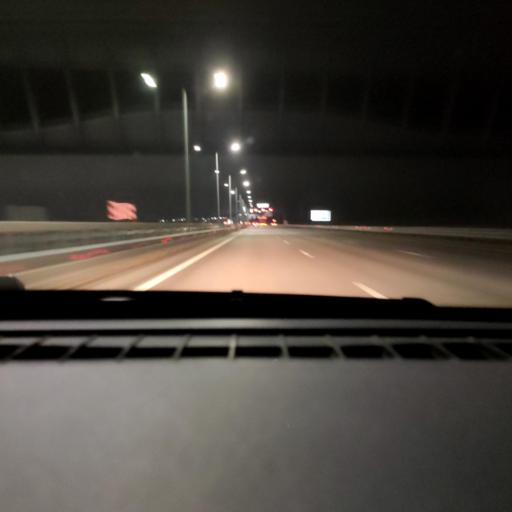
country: RU
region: Voronezj
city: Somovo
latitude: 51.7714
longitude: 39.3022
